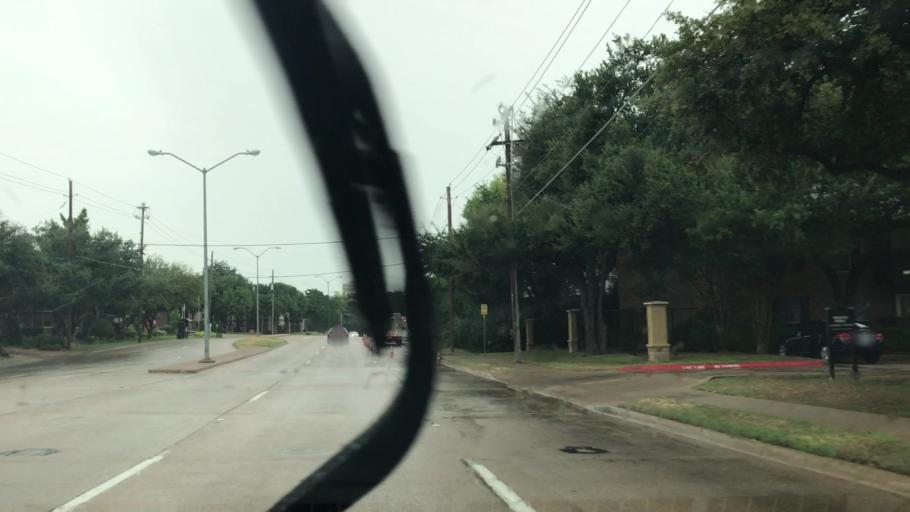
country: US
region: Texas
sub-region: Dallas County
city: Addison
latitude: 32.9388
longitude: -96.8078
